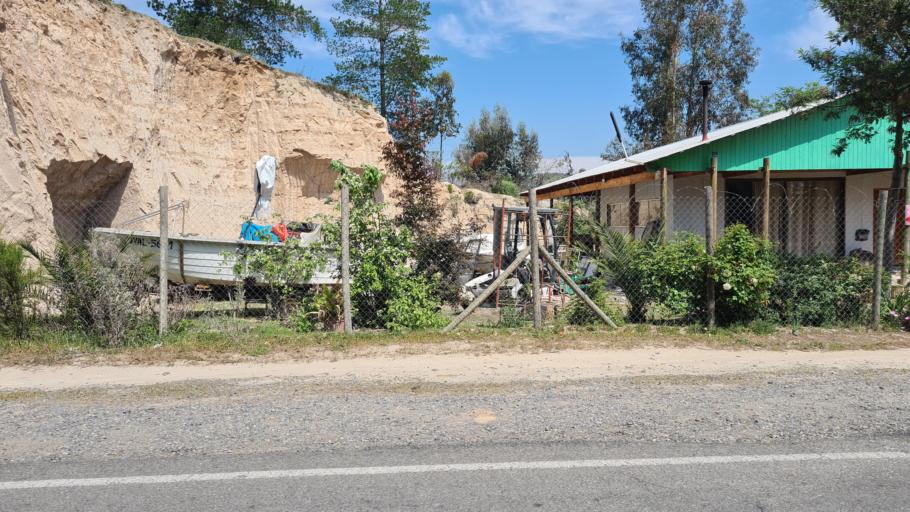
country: CL
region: O'Higgins
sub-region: Provincia de Cachapoal
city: San Vicente
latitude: -34.1596
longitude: -71.4138
